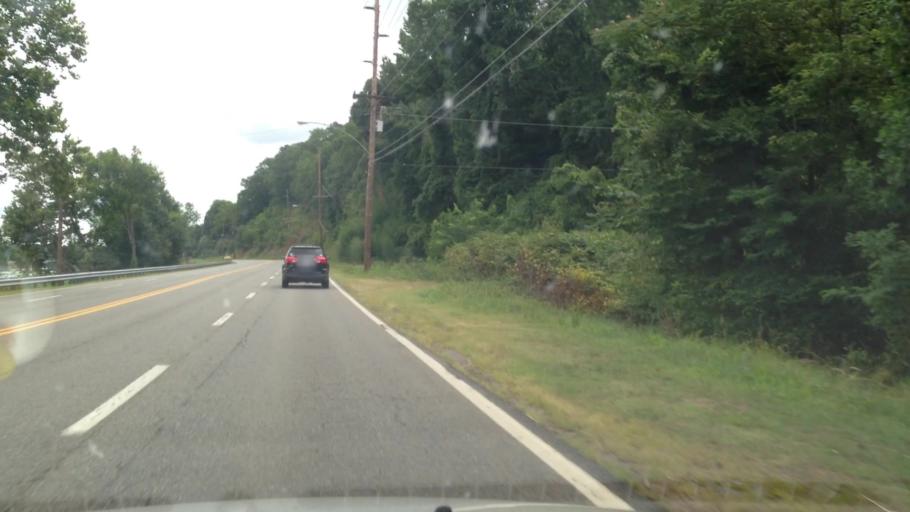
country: US
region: Virginia
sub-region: City of Danville
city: Danville
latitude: 36.5818
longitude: -79.4241
